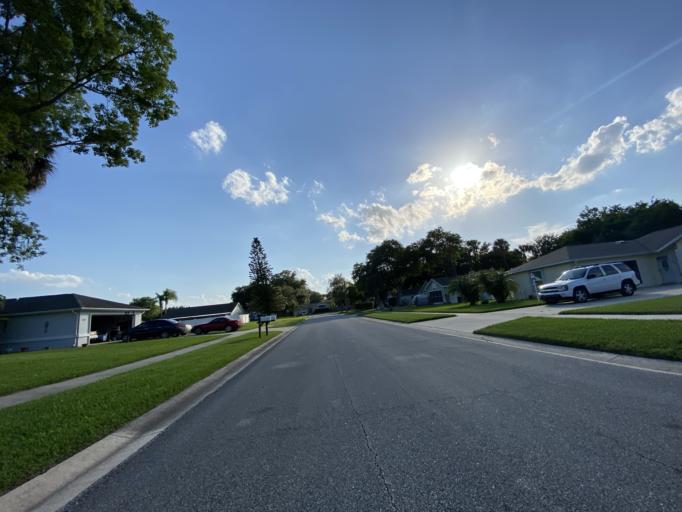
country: US
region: Florida
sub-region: Volusia County
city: Port Orange
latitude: 29.1475
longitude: -81.0109
